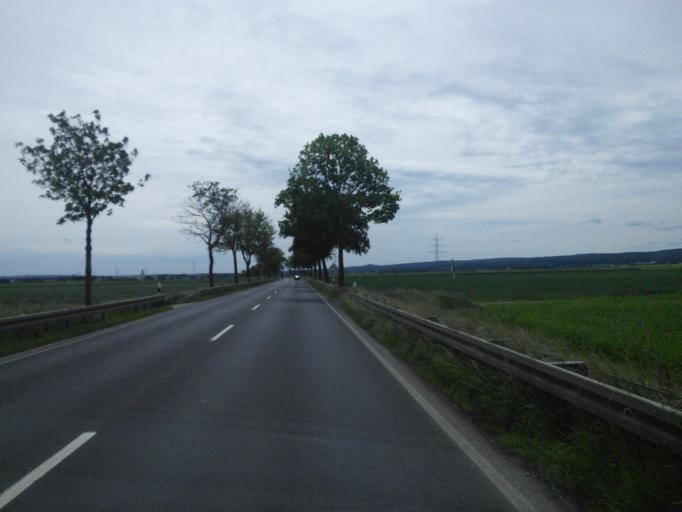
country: DE
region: North Rhine-Westphalia
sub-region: Regierungsbezirk Koln
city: Rheinbach
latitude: 50.6548
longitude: 6.8927
